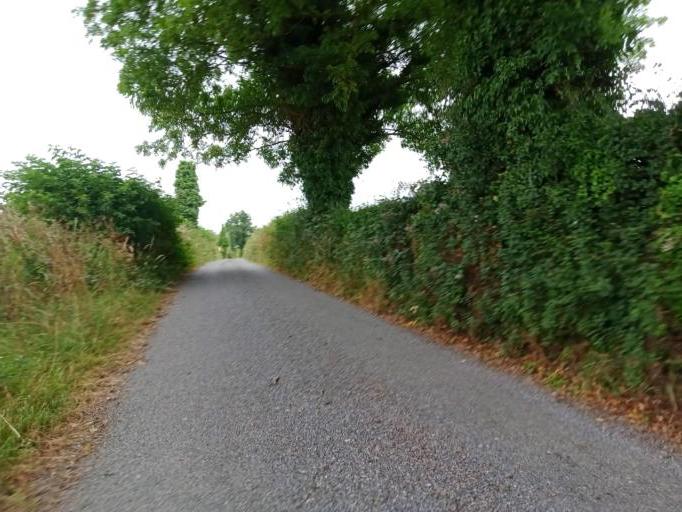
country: IE
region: Leinster
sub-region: Kilkenny
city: Callan
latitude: 52.5442
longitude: -7.4127
